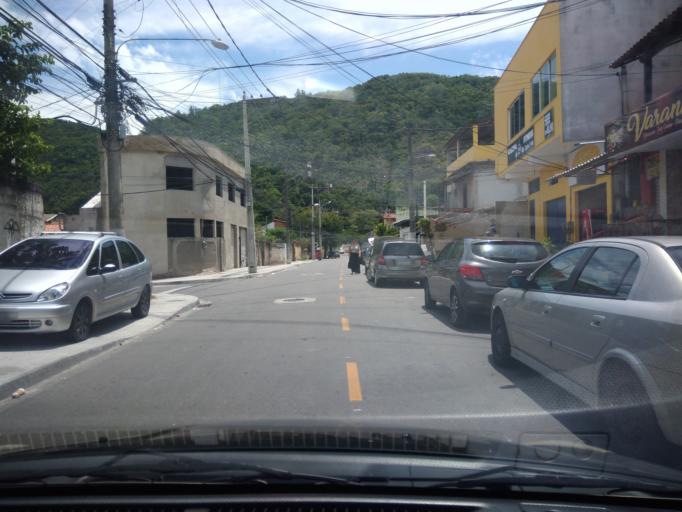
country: BR
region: Rio de Janeiro
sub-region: Niteroi
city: Niteroi
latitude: -22.9310
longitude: -43.0695
